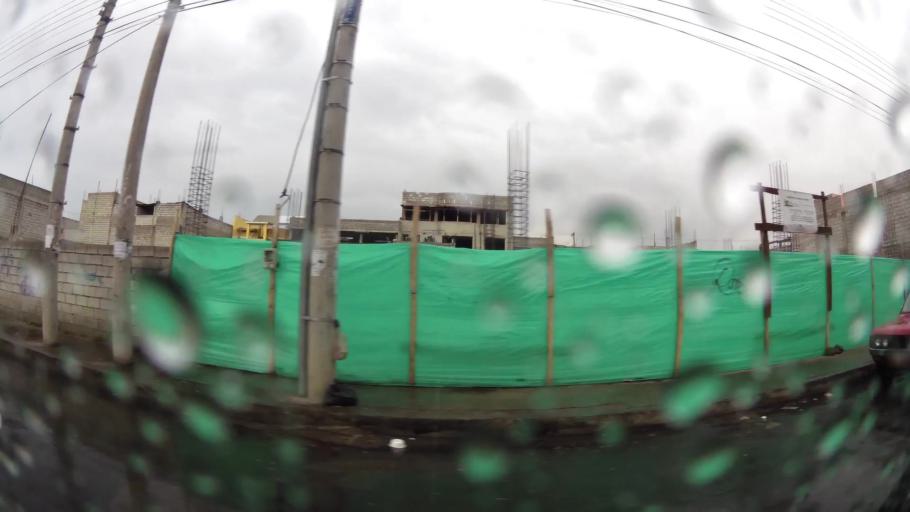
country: EC
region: Pichincha
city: Quito
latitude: -0.3100
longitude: -78.5494
